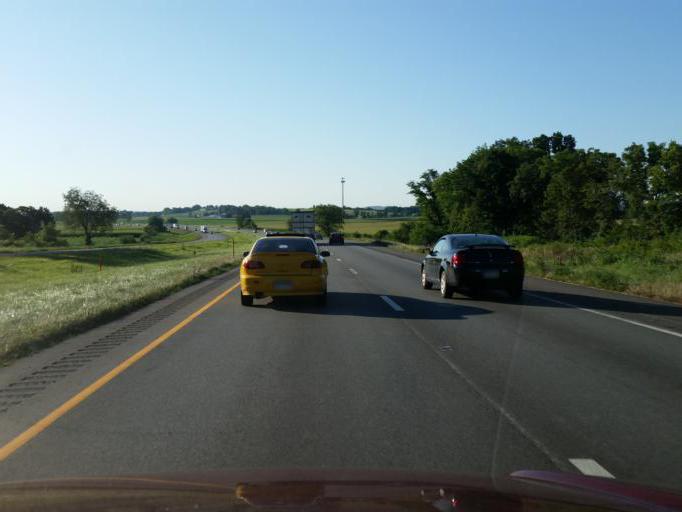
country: US
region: Pennsylvania
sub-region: Lancaster County
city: Rheems
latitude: 40.1361
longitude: -76.5460
